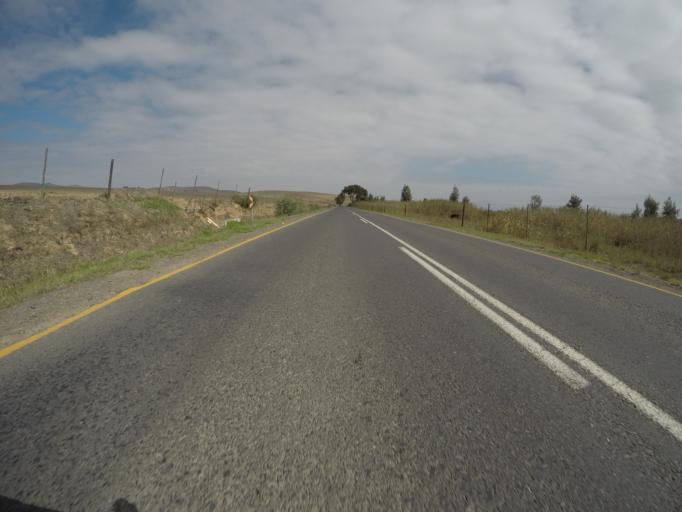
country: ZA
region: Western Cape
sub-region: City of Cape Town
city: Sunset Beach
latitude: -33.7842
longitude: 18.5556
